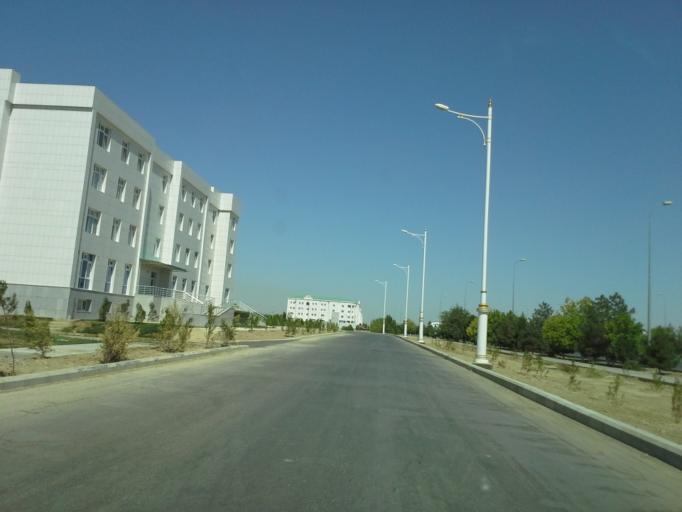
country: TM
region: Ahal
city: Ashgabat
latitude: 37.9838
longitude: 58.3308
